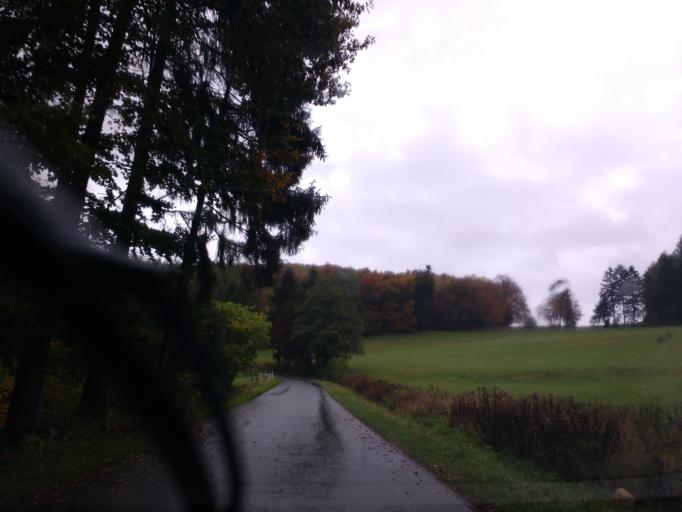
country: DE
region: Lower Saxony
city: Herzberg am Harz
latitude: 51.6334
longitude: 10.3873
